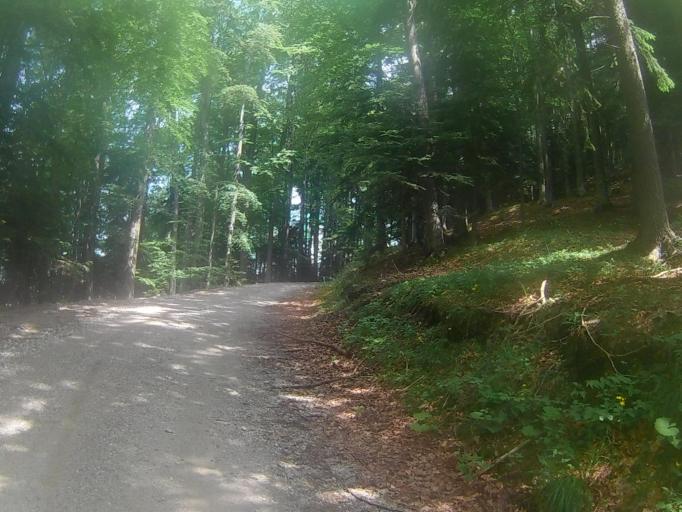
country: SI
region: Ruse
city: Bistrica ob Dravi
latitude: 46.5166
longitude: 15.5537
